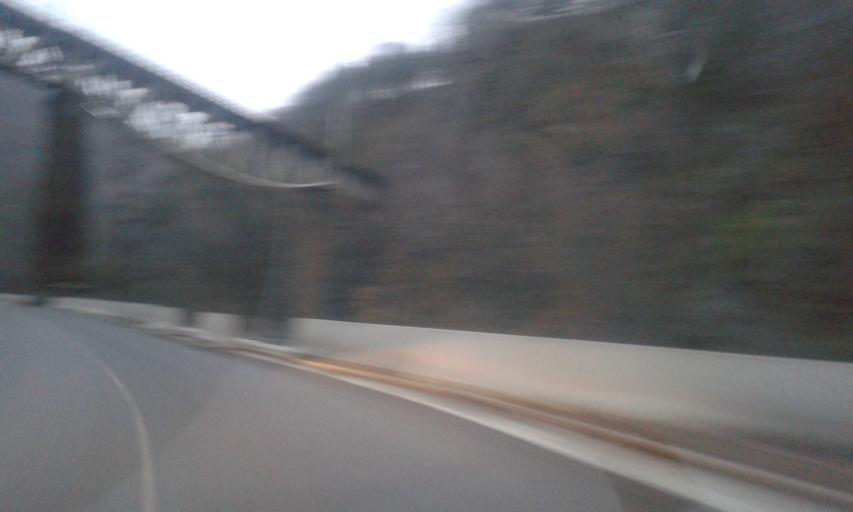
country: RO
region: Gorj
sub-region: Comuna Bumbesti-Jiu
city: Bumbesti-Jiu
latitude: 45.2052
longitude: 23.3739
